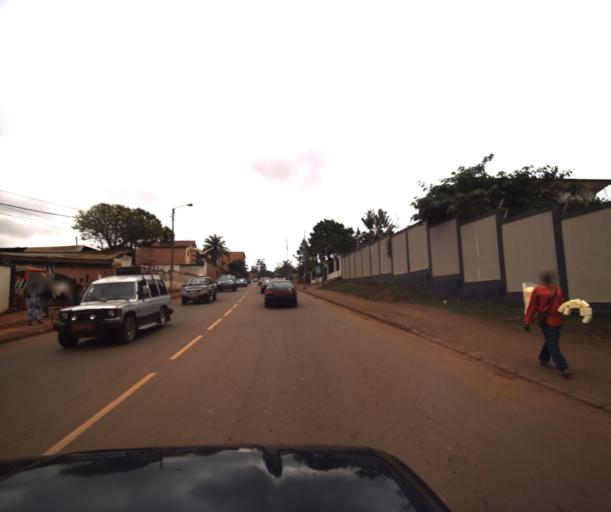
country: CM
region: Centre
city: Yaounde
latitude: 3.8379
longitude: 11.5152
